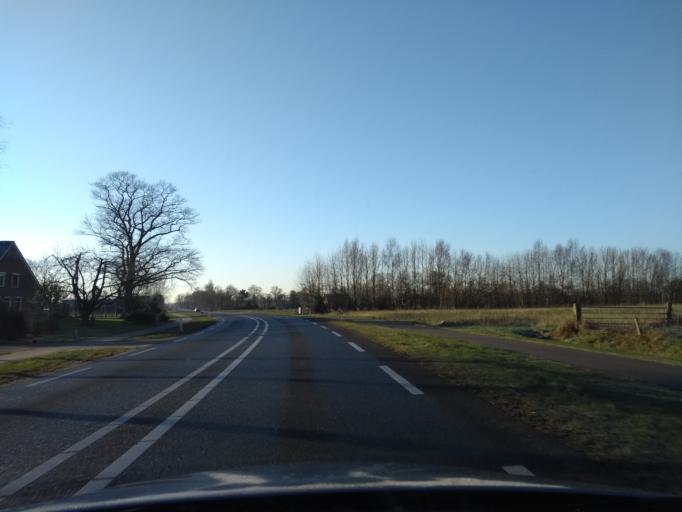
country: NL
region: Overijssel
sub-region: Gemeente Haaksbergen
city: Haaksbergen
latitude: 52.1925
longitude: 6.7356
